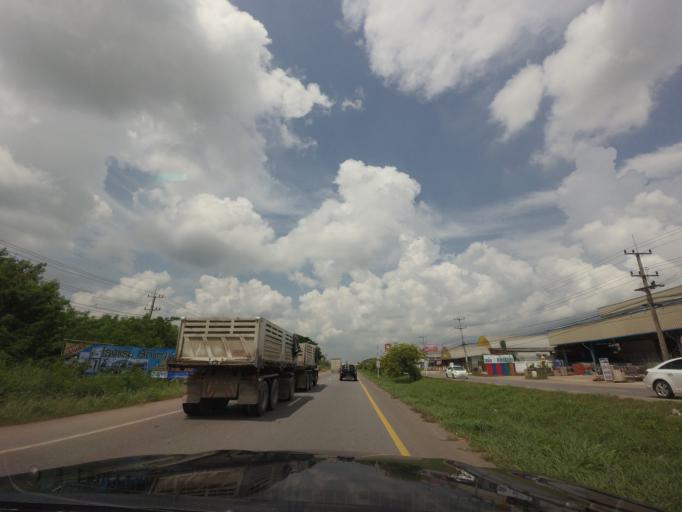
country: TH
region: Khon Kaen
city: Nong Ruea
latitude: 16.4899
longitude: 102.4484
